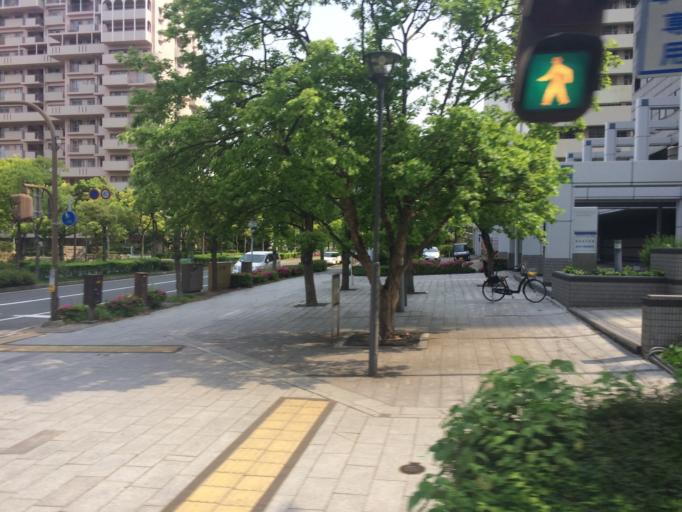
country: JP
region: Hyogo
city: Ashiya
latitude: 34.6902
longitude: 135.2712
